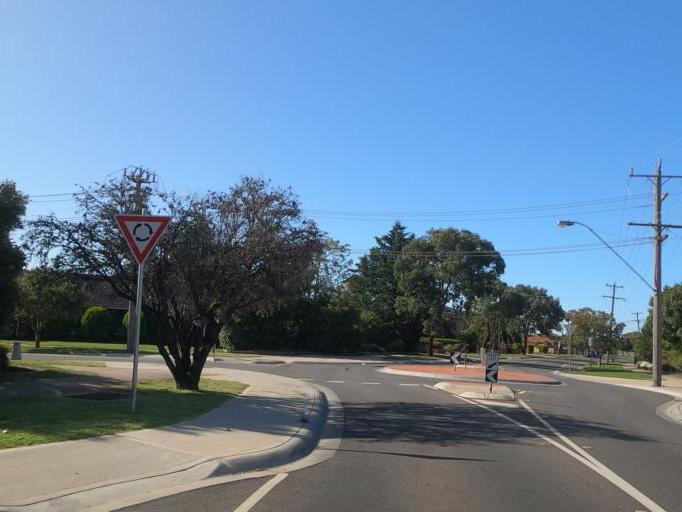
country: AU
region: Victoria
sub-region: Hume
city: Attwood
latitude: -37.6461
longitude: 144.8899
